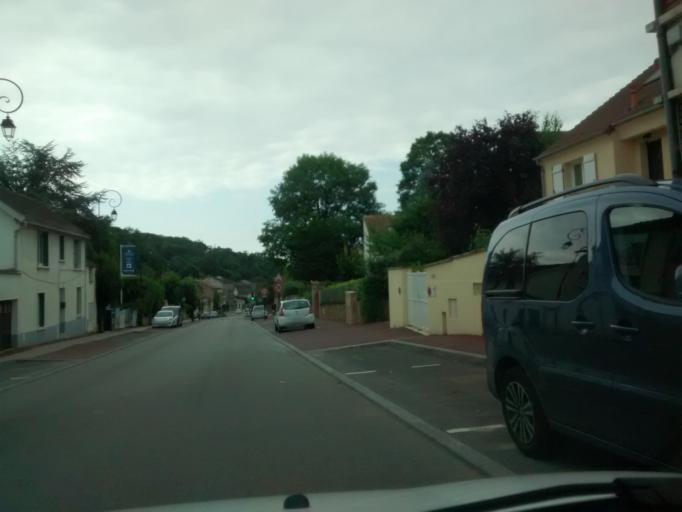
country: FR
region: Ile-de-France
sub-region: Departement des Yvelines
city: Buc
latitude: 48.7836
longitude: 2.1324
